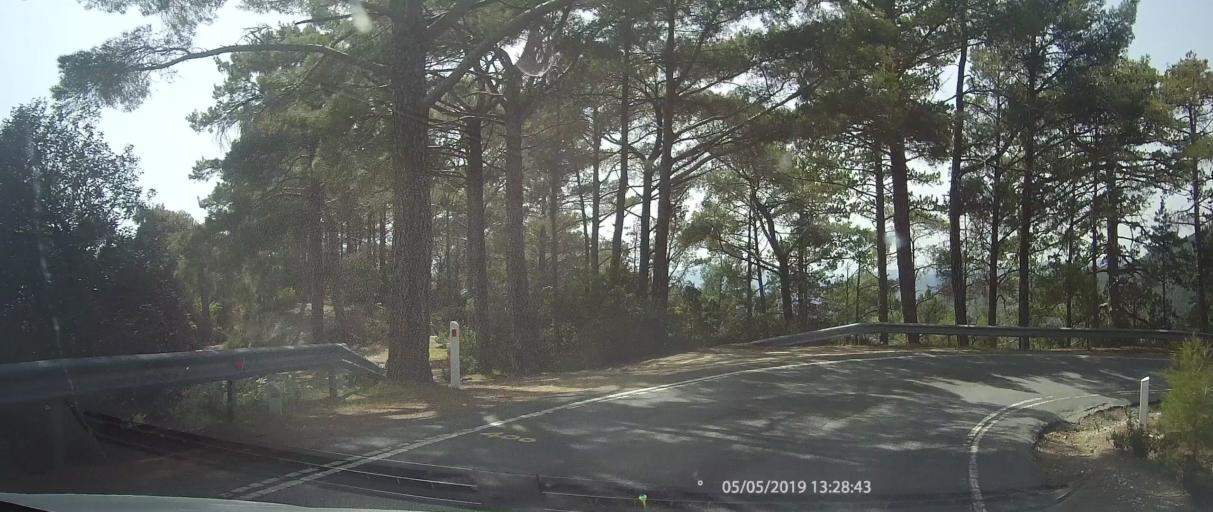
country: CY
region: Lefkosia
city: Kakopetria
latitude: 34.8966
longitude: 32.8520
